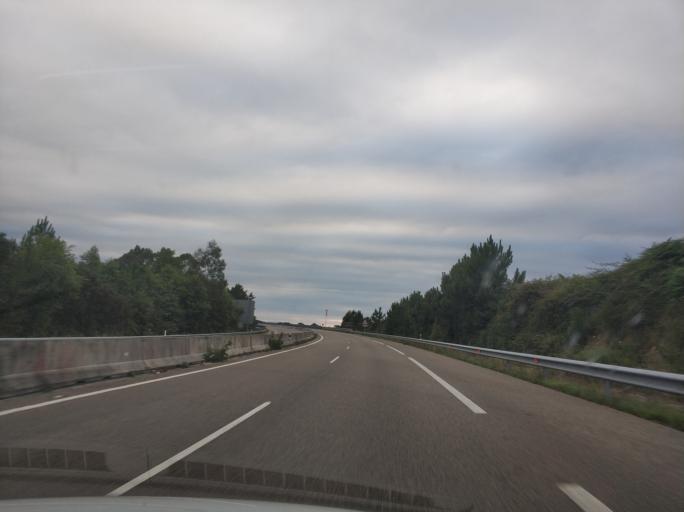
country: ES
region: Asturias
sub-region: Province of Asturias
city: Tineo
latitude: 43.5480
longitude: -6.4606
